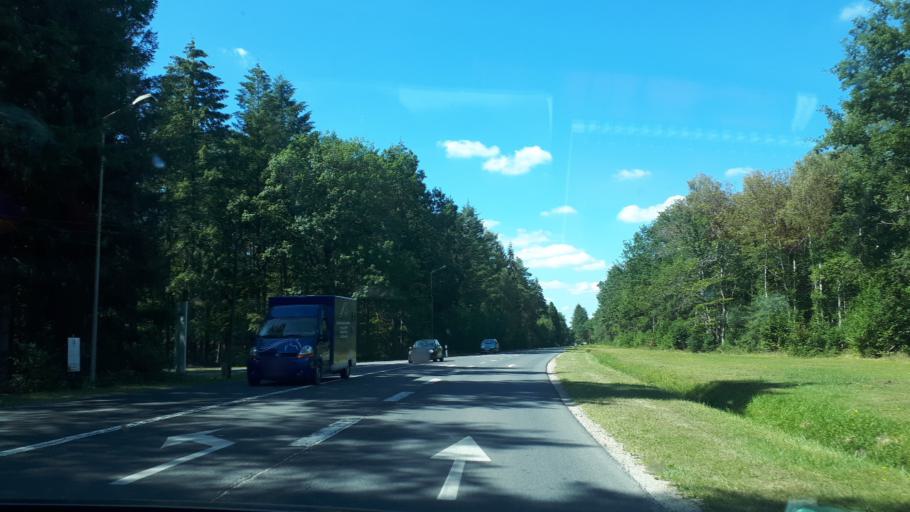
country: FR
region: Centre
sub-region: Departement du Loir-et-Cher
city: Lamotte-Beuvron
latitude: 47.5919
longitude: 2.0122
